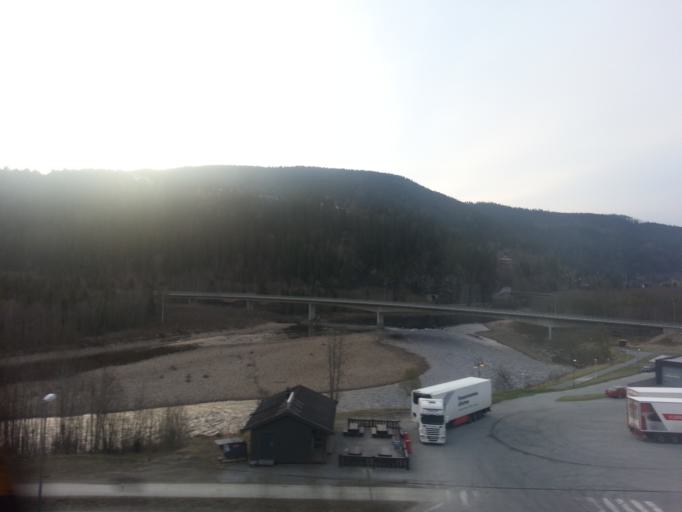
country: NO
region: Sor-Trondelag
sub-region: Midtre Gauldal
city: Storen
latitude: 63.0371
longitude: 10.2911
